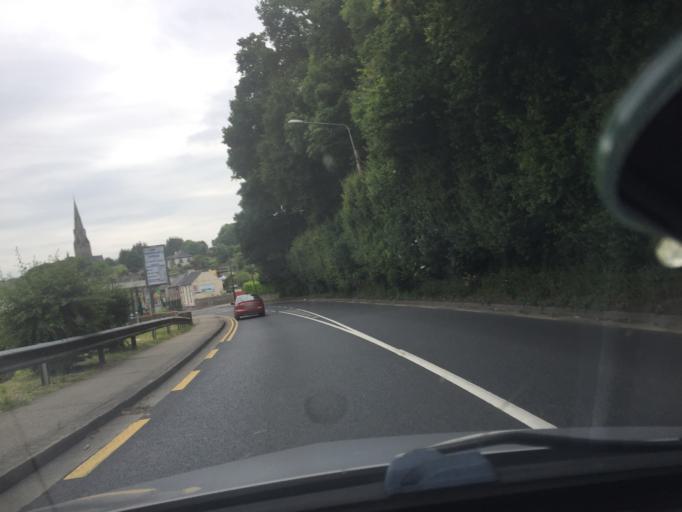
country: IE
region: Leinster
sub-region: Loch Garman
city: Enniscorthy
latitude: 52.5069
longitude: -6.5694
